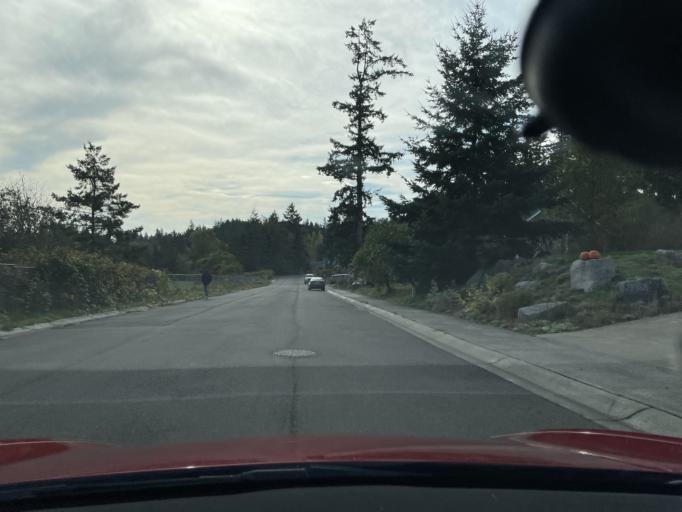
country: US
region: Washington
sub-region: San Juan County
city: Friday Harbor
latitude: 48.5419
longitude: -123.0302
